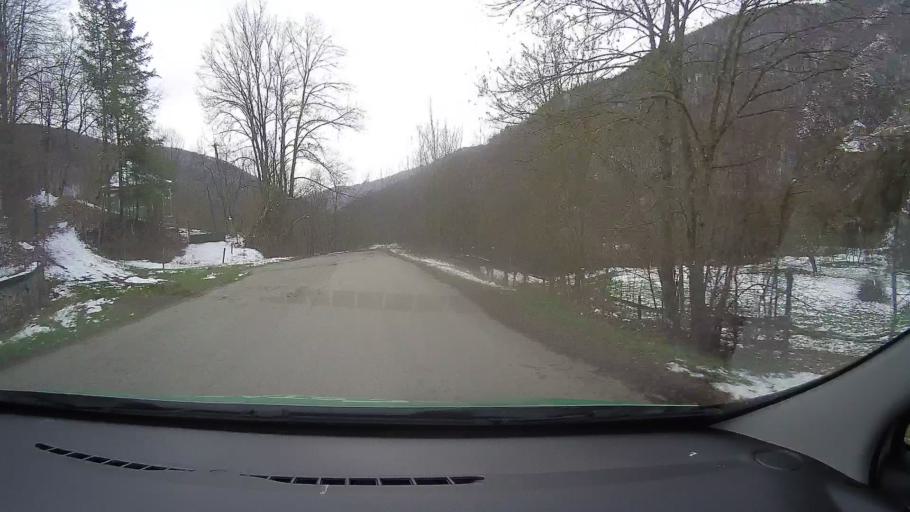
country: RO
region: Hunedoara
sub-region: Comuna Balsa
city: Balsa
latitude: 46.0169
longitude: 23.1486
